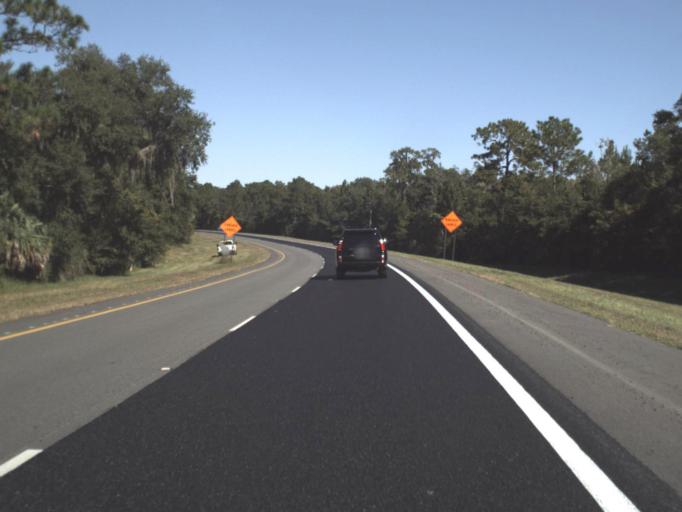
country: US
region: Florida
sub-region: Hernando County
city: Brookridge
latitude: 28.6281
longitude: -82.4900
